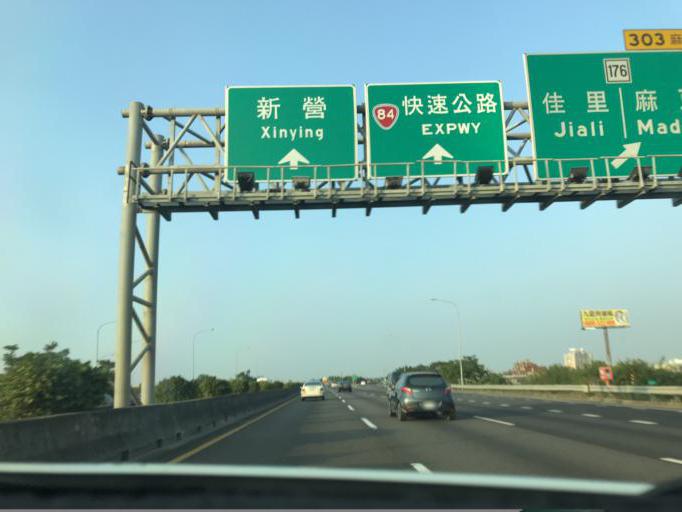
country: TW
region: Taiwan
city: Xinying
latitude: 23.1778
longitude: 120.2350
